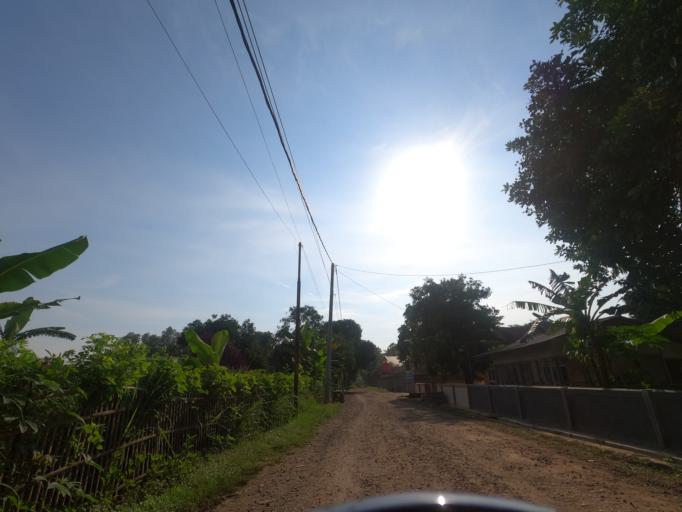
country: ID
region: West Java
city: Pamanukan
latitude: -6.5567
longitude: 107.8267
